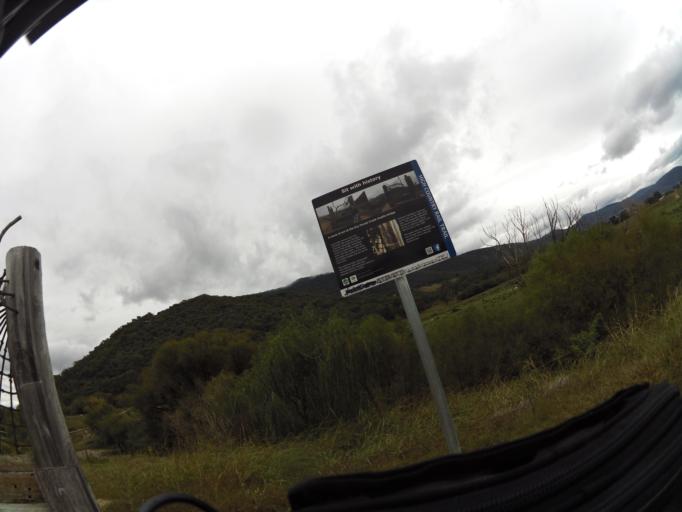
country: AU
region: New South Wales
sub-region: Albury Municipality
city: East Albury
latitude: -36.1835
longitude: 147.3426
